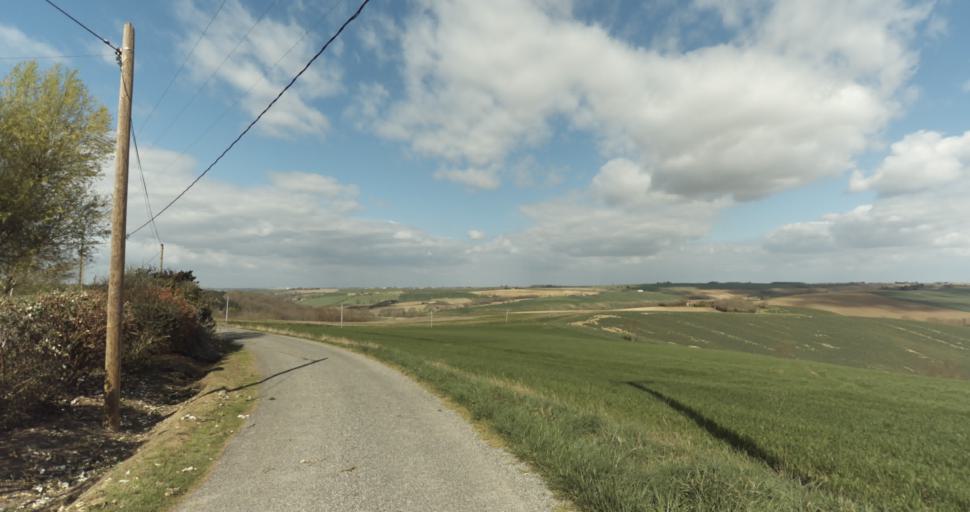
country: FR
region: Midi-Pyrenees
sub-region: Departement de la Haute-Garonne
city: Auterive
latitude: 43.3656
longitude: 1.5096
